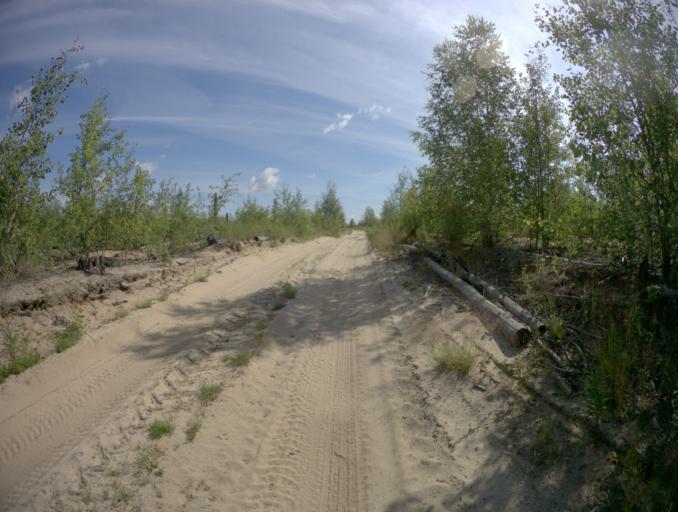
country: RU
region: Ivanovo
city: Talitsy
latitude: 56.5123
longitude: 42.3902
